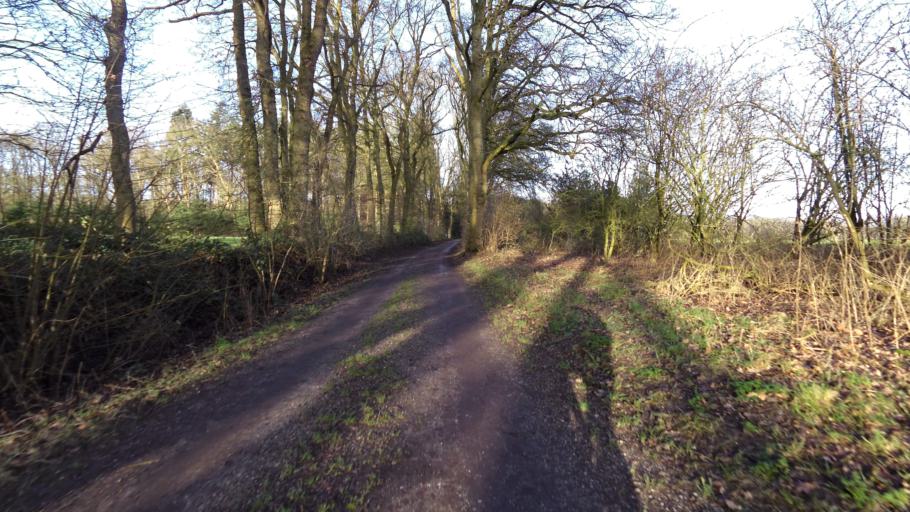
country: NL
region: Gelderland
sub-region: Gemeente Epe
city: Vaassen
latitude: 52.2571
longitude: 5.9263
